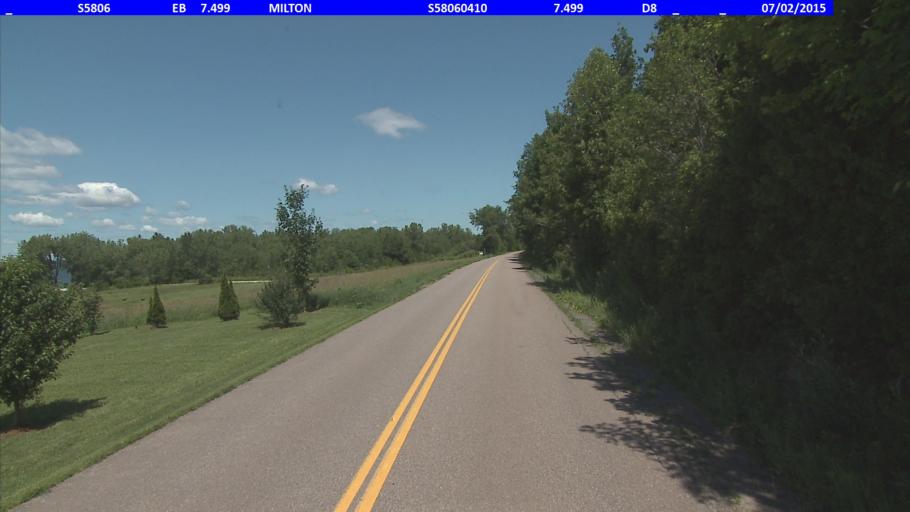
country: US
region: Vermont
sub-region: Chittenden County
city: Milton
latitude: 44.7041
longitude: -73.2064
